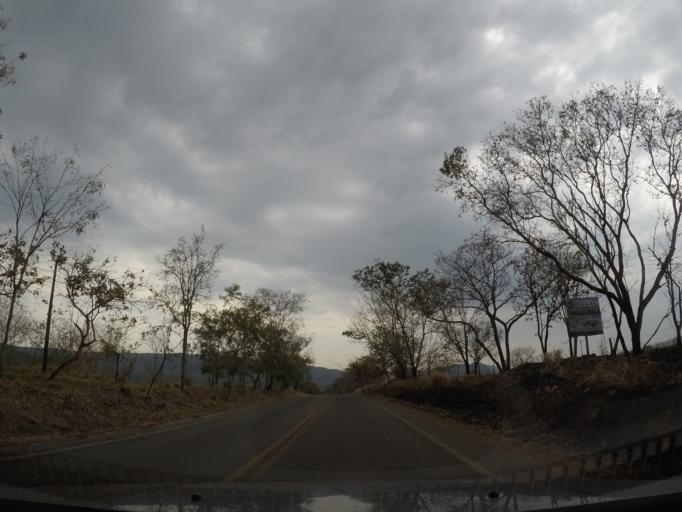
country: BR
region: Goias
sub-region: Pirenopolis
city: Pirenopolis
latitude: -15.8517
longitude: -48.9345
